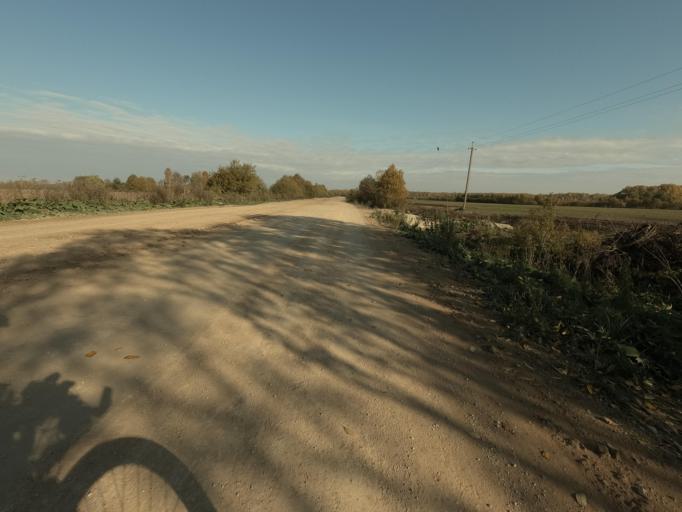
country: RU
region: Novgorod
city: Batetskiy
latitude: 58.8151
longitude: 30.6985
